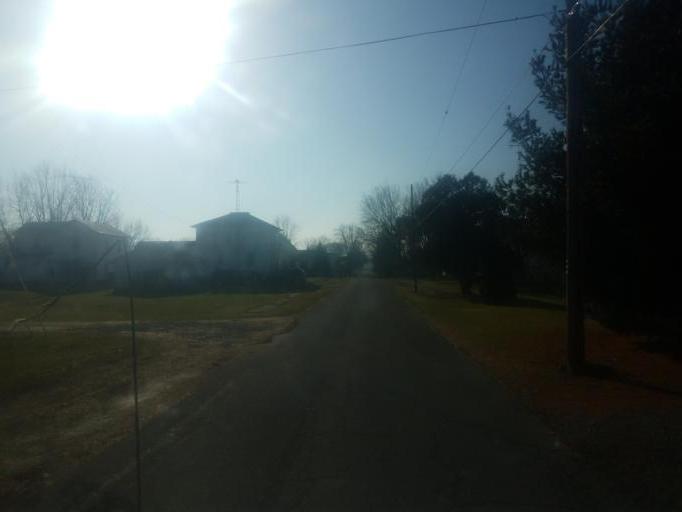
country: US
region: Ohio
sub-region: Seneca County
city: Tiffin
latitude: 41.0516
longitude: -83.0106
